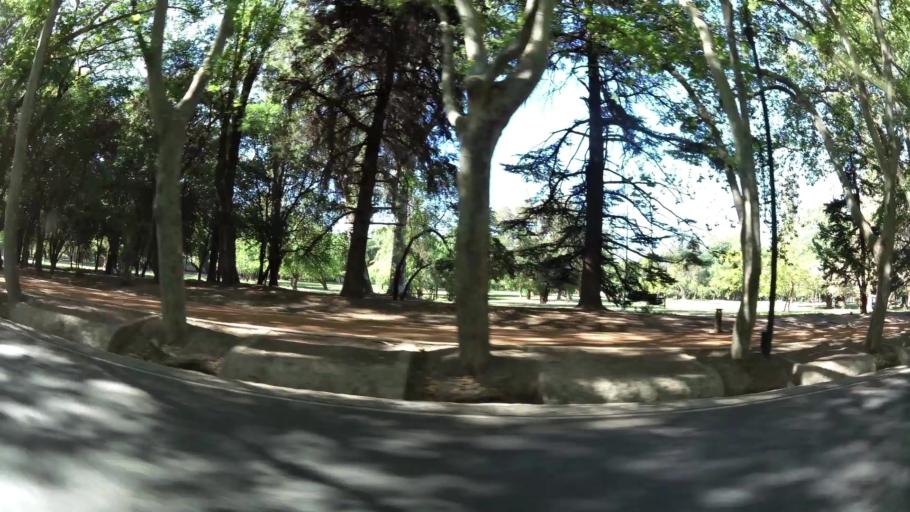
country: AR
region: Mendoza
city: Mendoza
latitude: -32.8889
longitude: -68.8650
